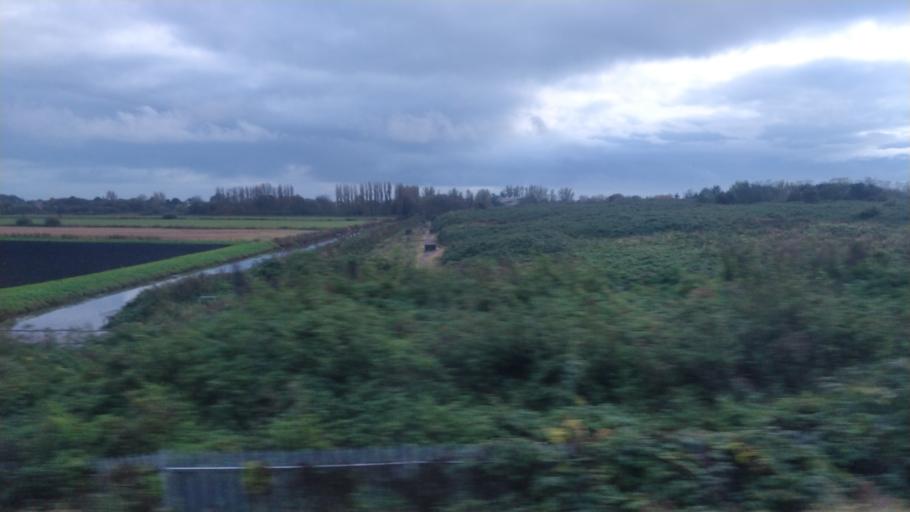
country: GB
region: England
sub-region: Sefton
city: Southport
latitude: 53.6366
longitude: -2.9633
